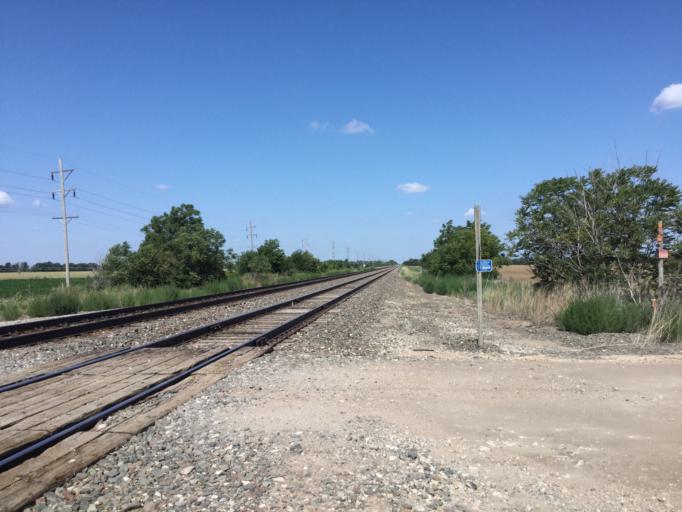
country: US
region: Kansas
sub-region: Harvey County
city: Halstead
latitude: 38.0208
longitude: -97.6471
